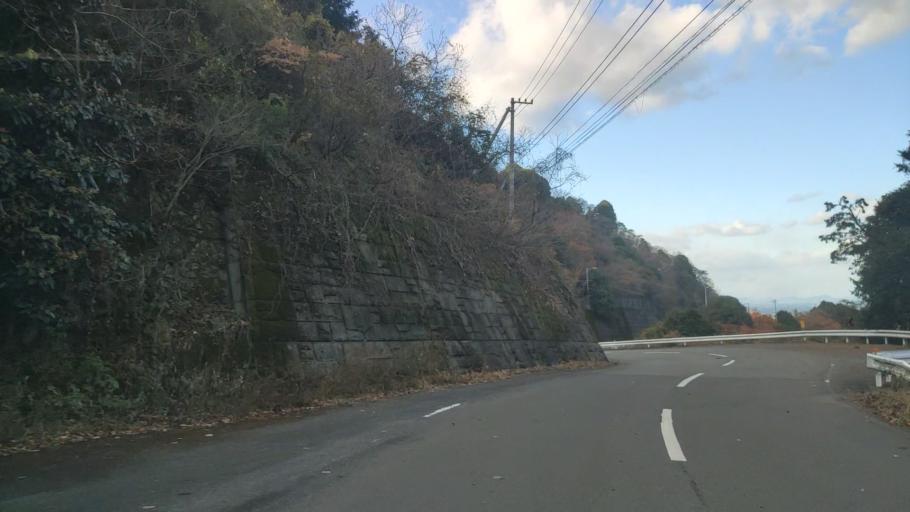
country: JP
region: Ehime
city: Saijo
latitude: 33.8807
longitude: 133.1328
